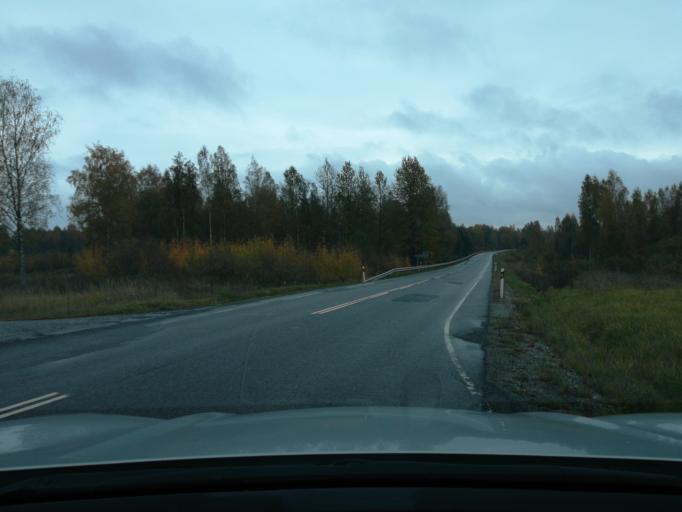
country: EE
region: Ida-Virumaa
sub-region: Johvi vald
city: Johvi
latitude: 59.1924
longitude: 27.5550
